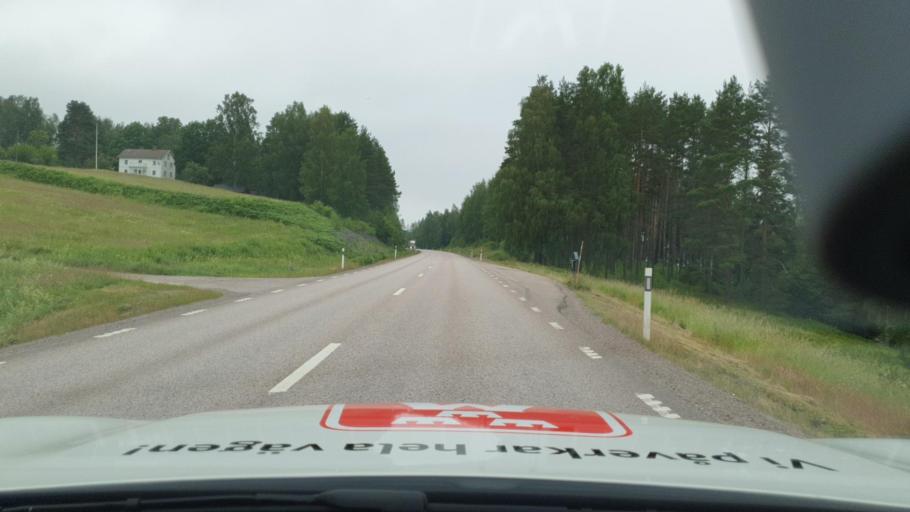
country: SE
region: Vaermland
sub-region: Sunne Kommun
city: Sunne
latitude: 59.9187
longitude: 13.1327
